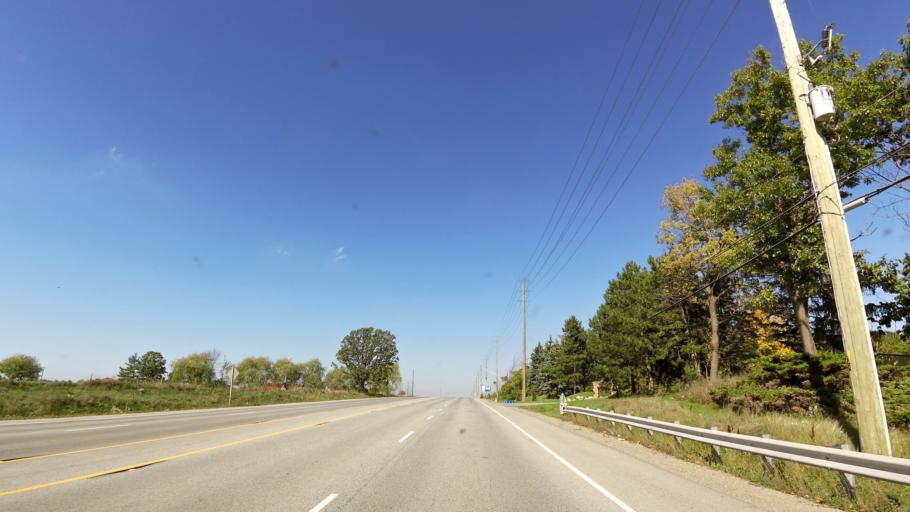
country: CA
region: Ontario
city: Burlington
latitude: 43.4567
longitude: -79.8036
